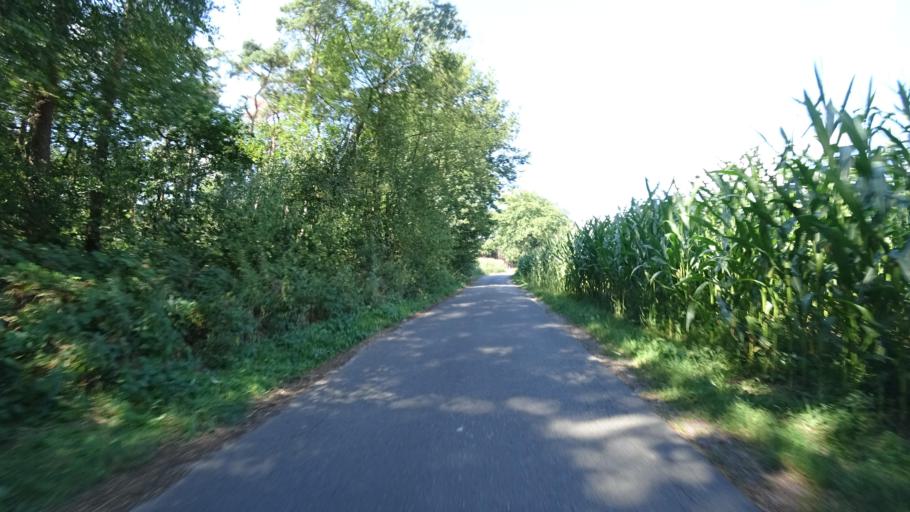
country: DE
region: North Rhine-Westphalia
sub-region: Regierungsbezirk Detmold
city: Guetersloh
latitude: 51.9280
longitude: 8.3957
